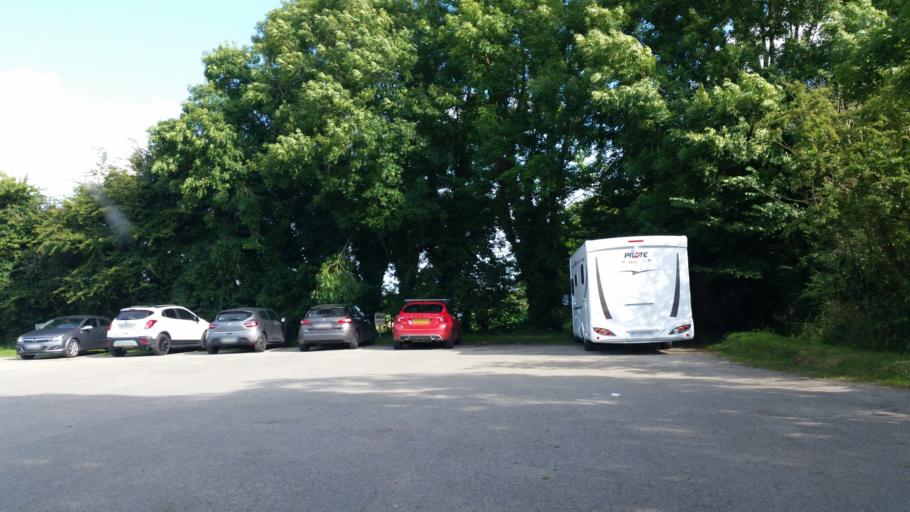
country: FR
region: Lower Normandy
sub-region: Departement de la Manche
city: Sainte-Mere-Eglise
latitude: 49.4604
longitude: -1.3061
